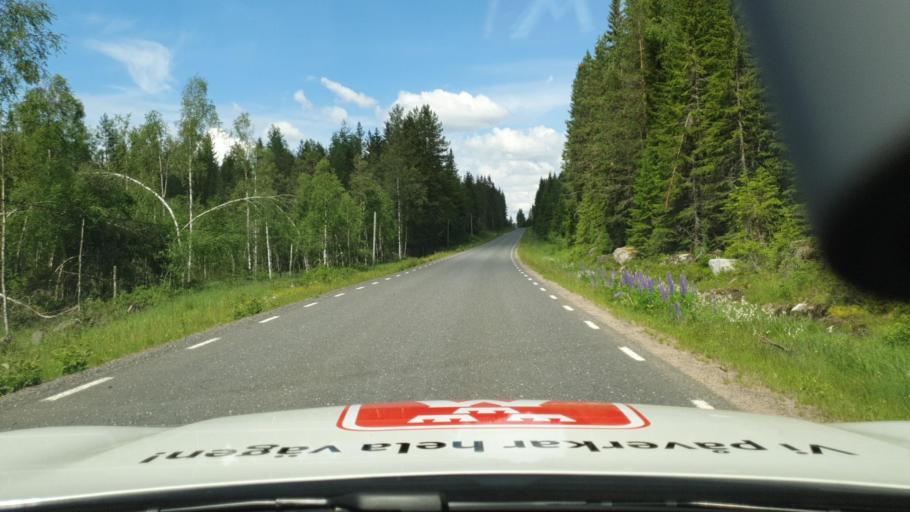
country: SE
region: Vaermland
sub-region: Torsby Kommun
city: Torsby
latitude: 60.5235
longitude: 12.8255
